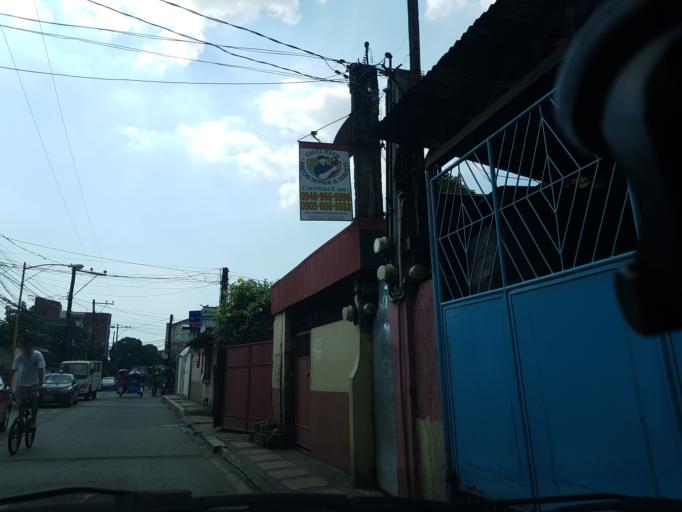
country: PH
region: Calabarzon
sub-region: Province of Rizal
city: Pateros
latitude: 14.5641
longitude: 121.0887
